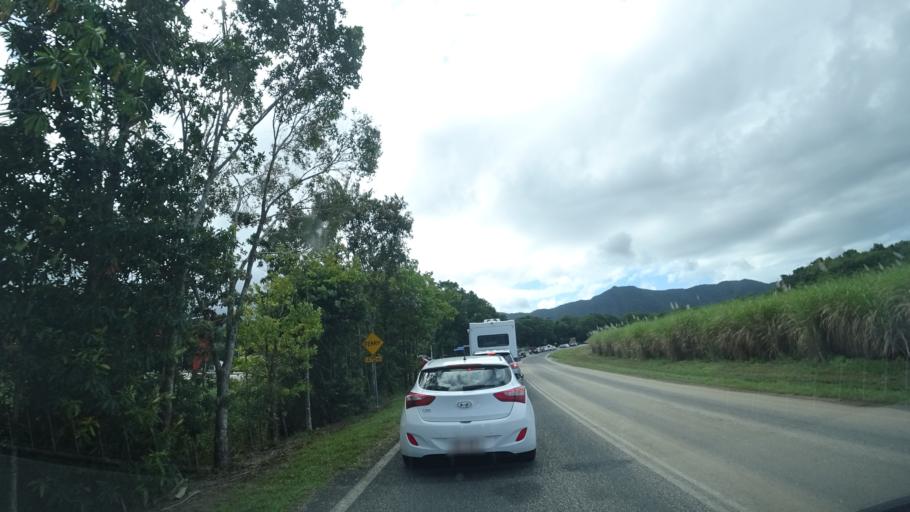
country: AU
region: Queensland
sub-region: Cairns
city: Port Douglas
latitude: -16.2629
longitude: 145.3930
